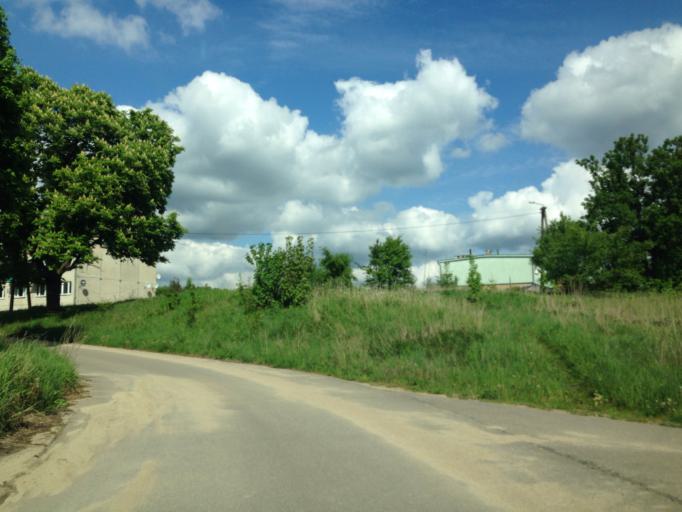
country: PL
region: Warmian-Masurian Voivodeship
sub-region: Powiat nidzicki
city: Nidzica
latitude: 53.4742
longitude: 20.3910
